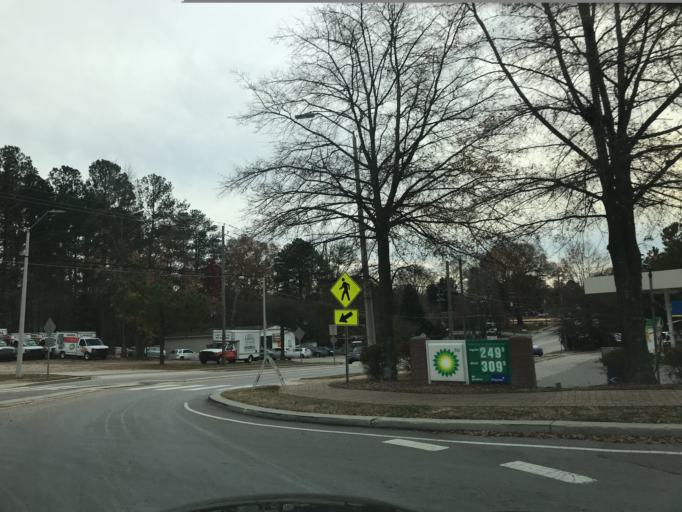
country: US
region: North Carolina
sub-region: Wake County
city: Cary
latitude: 35.7902
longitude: -78.7723
